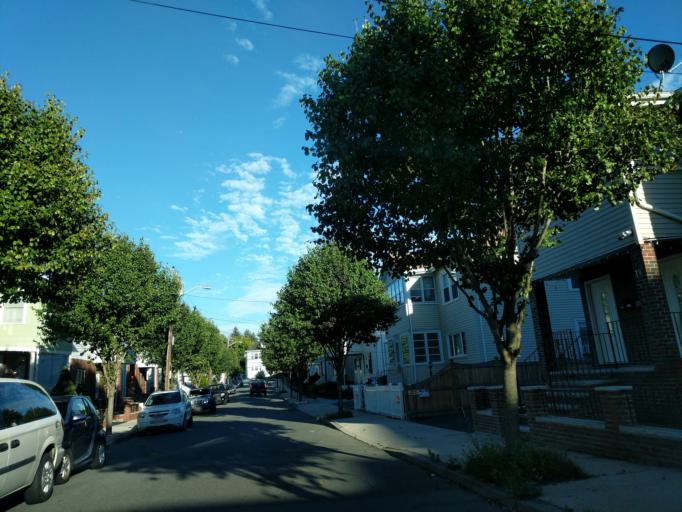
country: US
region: Massachusetts
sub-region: Middlesex County
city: Everett
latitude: 42.4112
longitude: -71.0449
